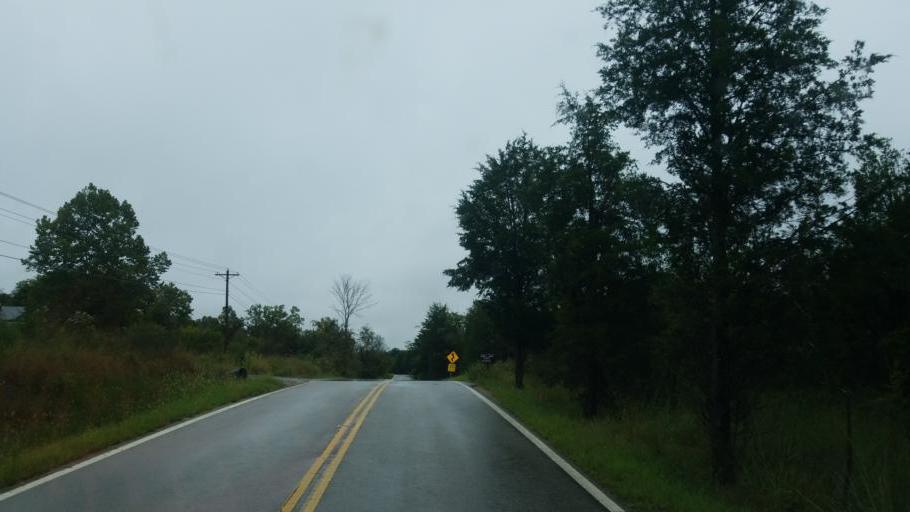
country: US
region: Ohio
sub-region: Adams County
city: West Union
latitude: 38.7742
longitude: -83.5331
